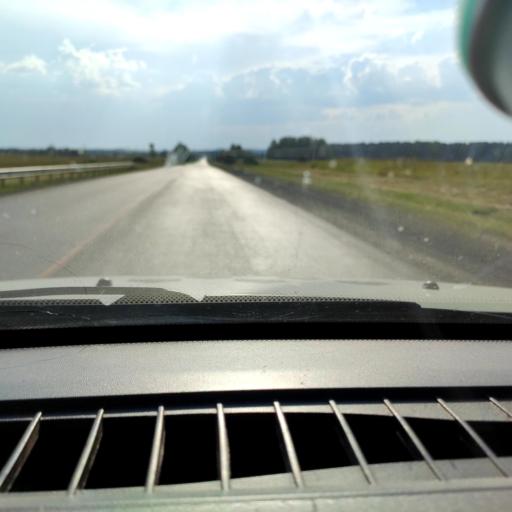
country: RU
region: Udmurtiya
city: Debesy
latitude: 57.6967
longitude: 54.0130
